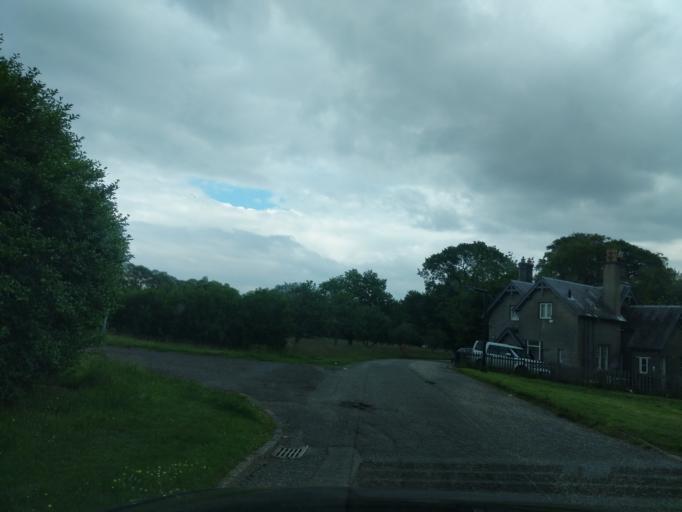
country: GB
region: Scotland
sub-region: Midlothian
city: Penicuik
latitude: 55.8602
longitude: -3.2086
